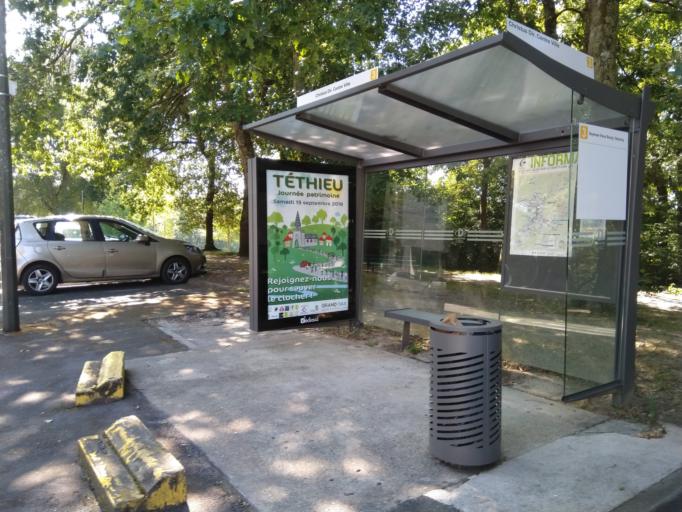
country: FR
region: Aquitaine
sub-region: Departement des Landes
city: Saint-Paul-les-Dax
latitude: 43.7292
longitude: -1.0659
